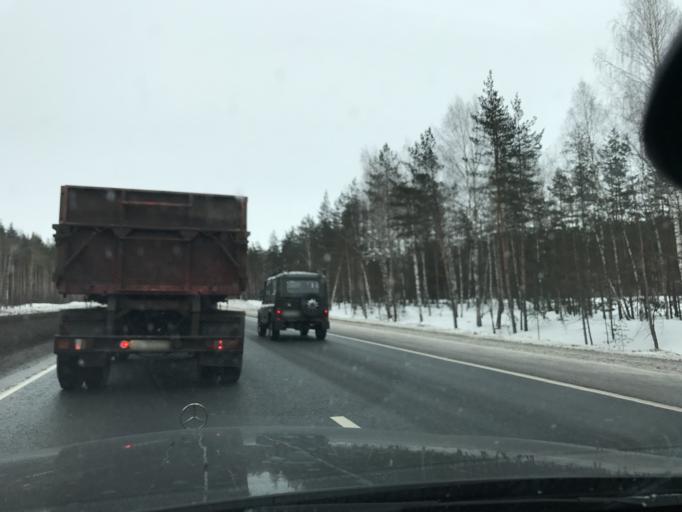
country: RU
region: Nizjnij Novgorod
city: Pyra
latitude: 56.2950
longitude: 43.3966
